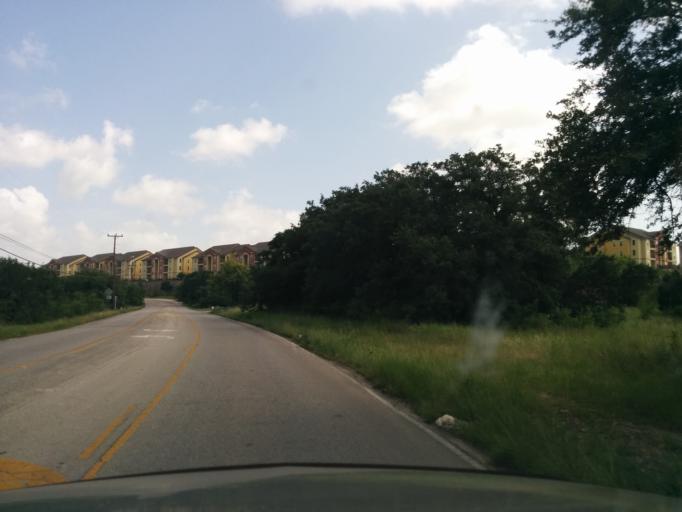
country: US
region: Texas
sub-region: Bexar County
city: Cross Mountain
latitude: 29.5928
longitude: -98.6289
